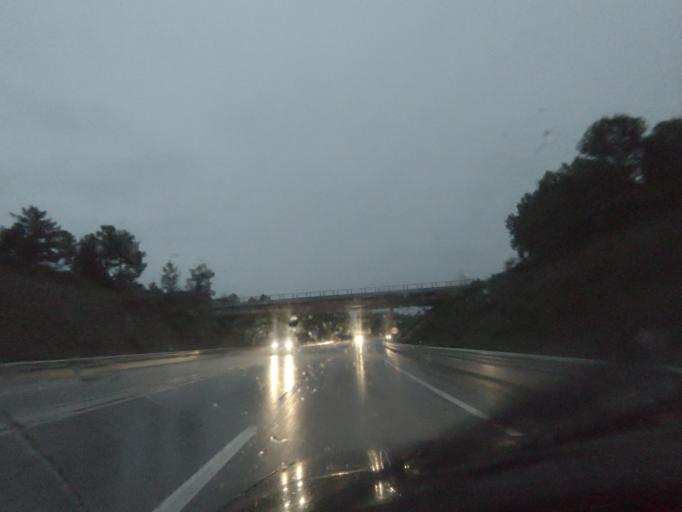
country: PT
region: Vila Real
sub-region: Sabrosa
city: Vilela
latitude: 41.2663
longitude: -7.6470
